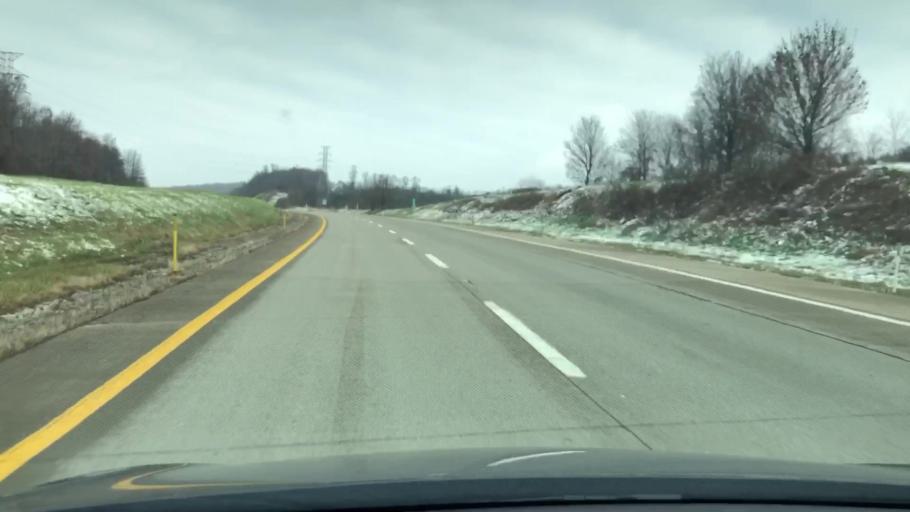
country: US
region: Pennsylvania
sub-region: Westmoreland County
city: Greensburg
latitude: 40.3529
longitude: -79.5628
